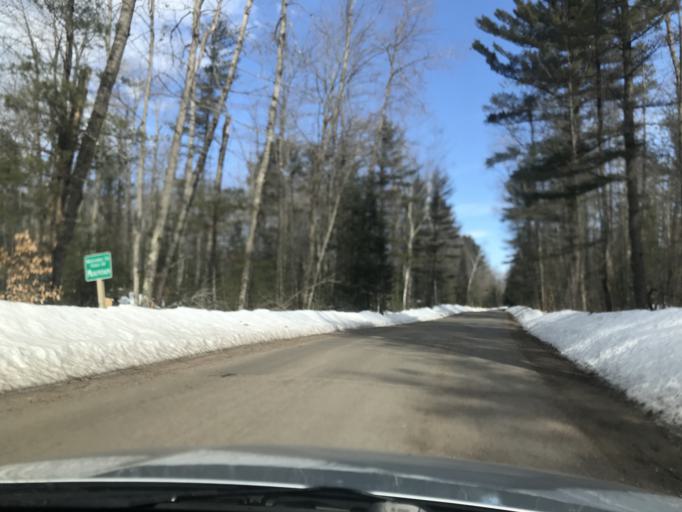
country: US
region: Wisconsin
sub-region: Menominee County
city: Legend Lake
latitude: 45.1170
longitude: -88.4463
